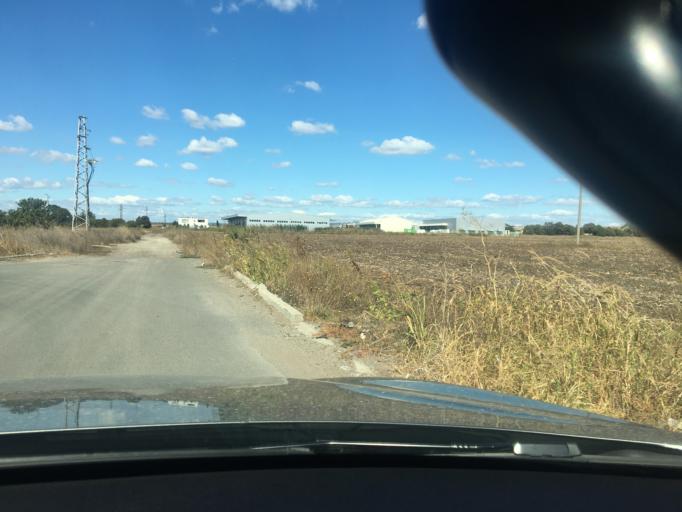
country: BG
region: Burgas
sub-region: Obshtina Burgas
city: Burgas
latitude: 42.5353
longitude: 27.4519
